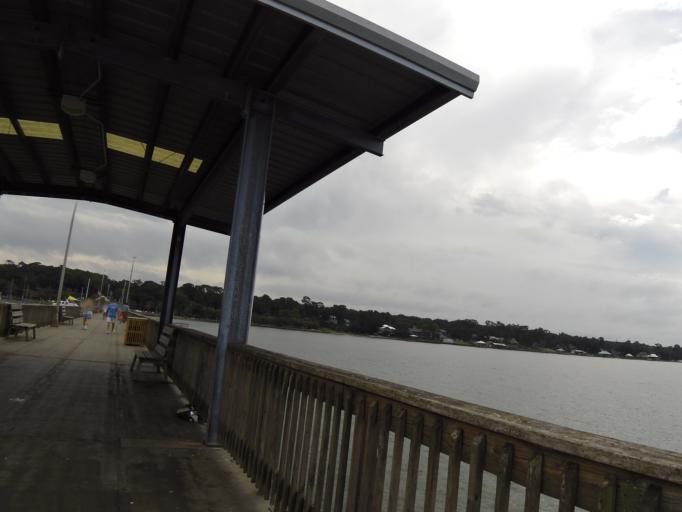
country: US
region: Alabama
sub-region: Baldwin County
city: Fairhope
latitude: 30.5256
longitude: -87.9168
